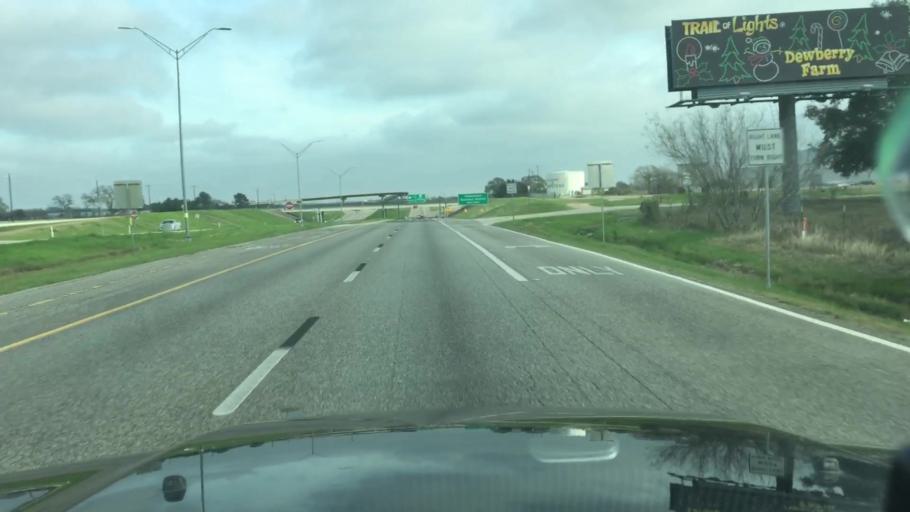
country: US
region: Texas
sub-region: Waller County
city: Hempstead
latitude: 30.1163
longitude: -96.0848
